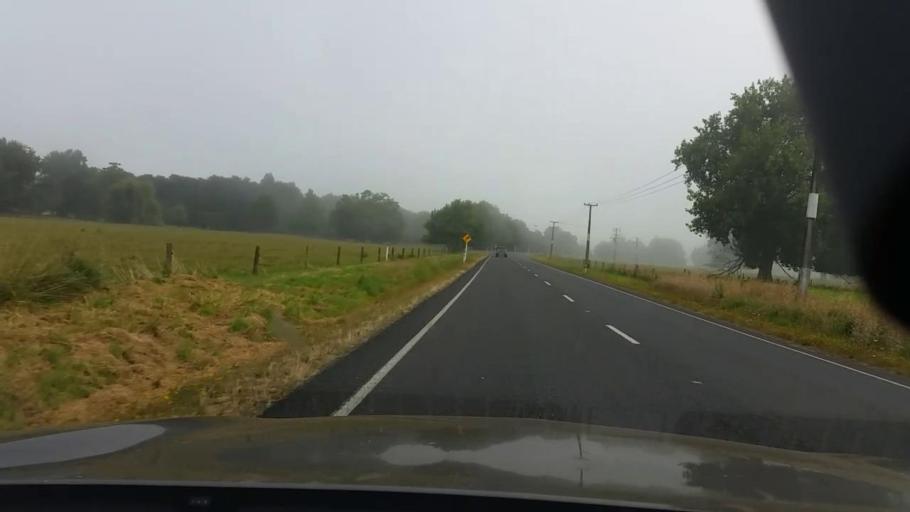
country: NZ
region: Waikato
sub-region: Hamilton City
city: Hamilton
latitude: -37.6435
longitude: 175.2953
